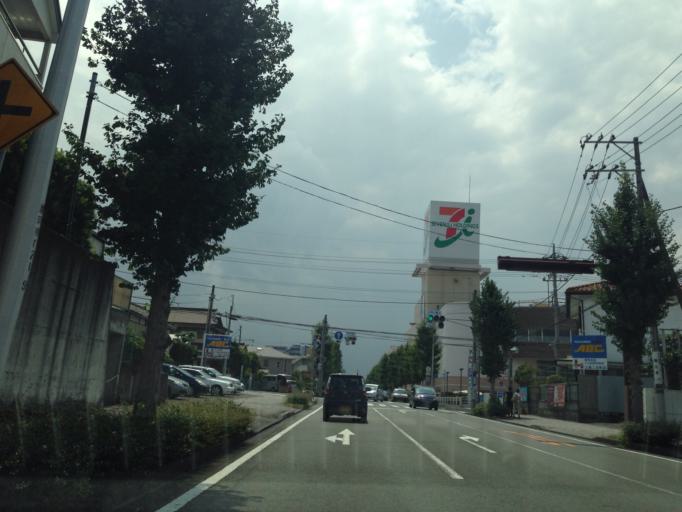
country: JP
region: Shizuoka
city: Mishima
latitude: 35.1149
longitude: 138.9197
